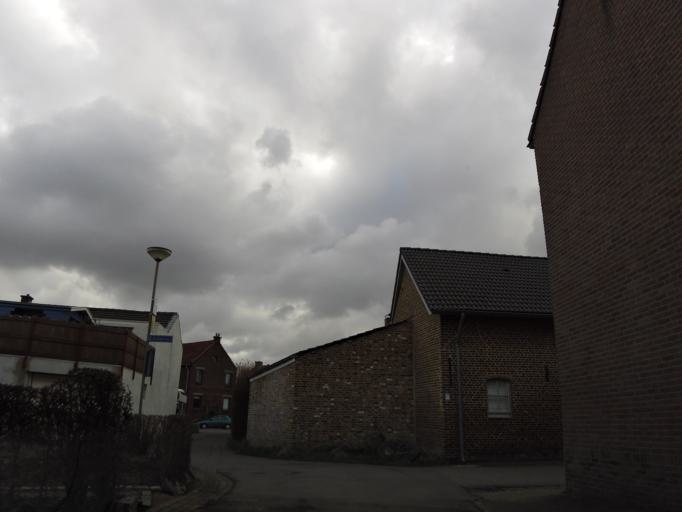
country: NL
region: Limburg
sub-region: Gemeente Stein
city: Stein
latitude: 50.9609
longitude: 5.7379
